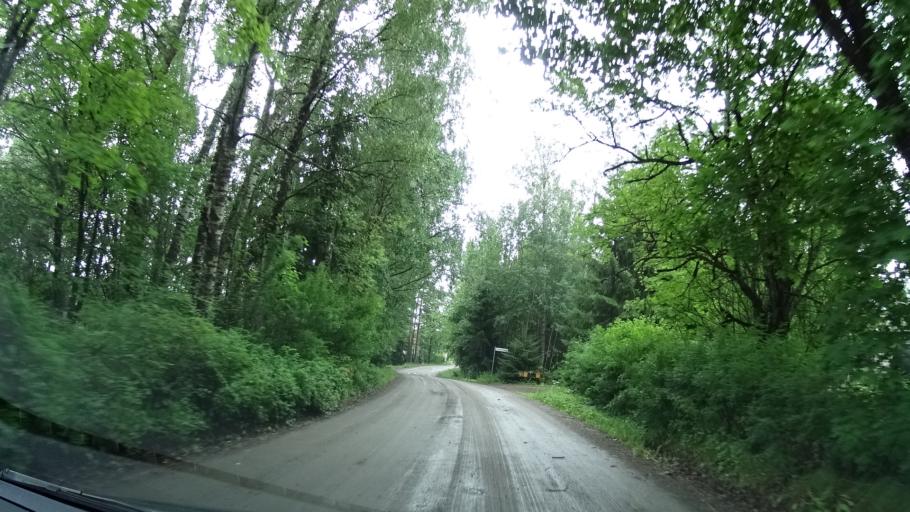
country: FI
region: Pirkanmaa
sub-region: Lounais-Pirkanmaa
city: Punkalaidun
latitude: 61.1130
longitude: 23.2835
